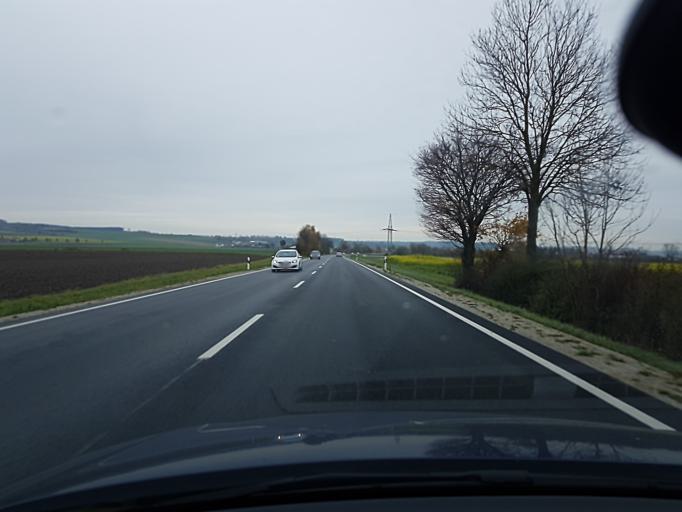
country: DE
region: Bavaria
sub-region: Lower Bavaria
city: Essenbach
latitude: 48.6003
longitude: 12.2020
